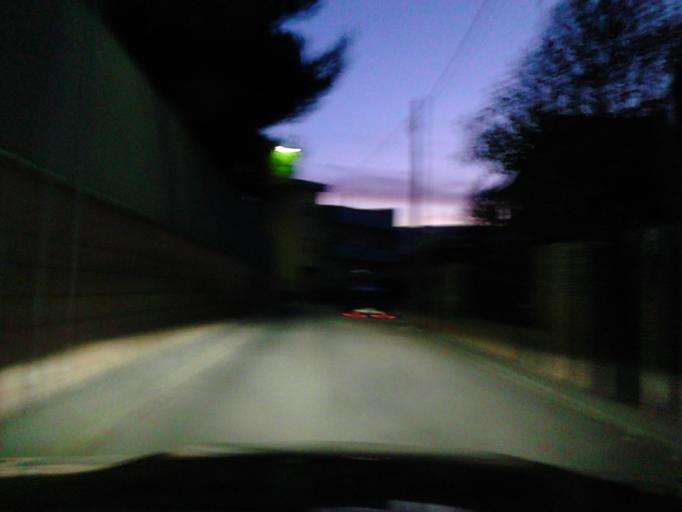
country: IT
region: Apulia
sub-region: Provincia di Bari
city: Sannicandro di Bari
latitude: 41.0002
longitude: 16.8046
